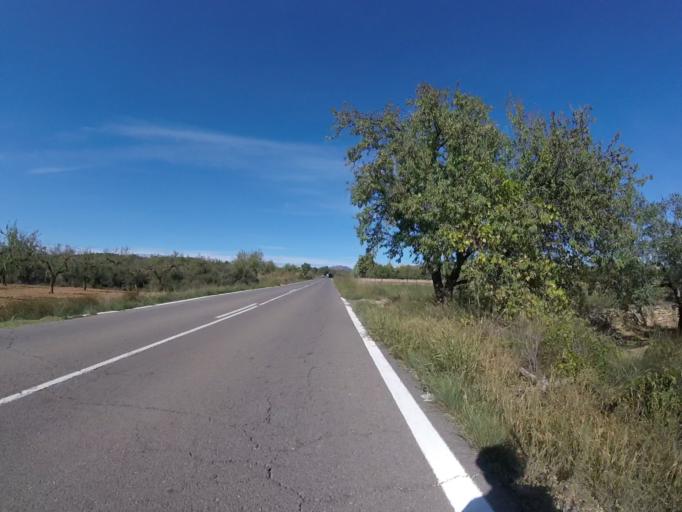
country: ES
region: Valencia
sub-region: Provincia de Castello
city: Benlloch
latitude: 40.2189
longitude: 0.0161
